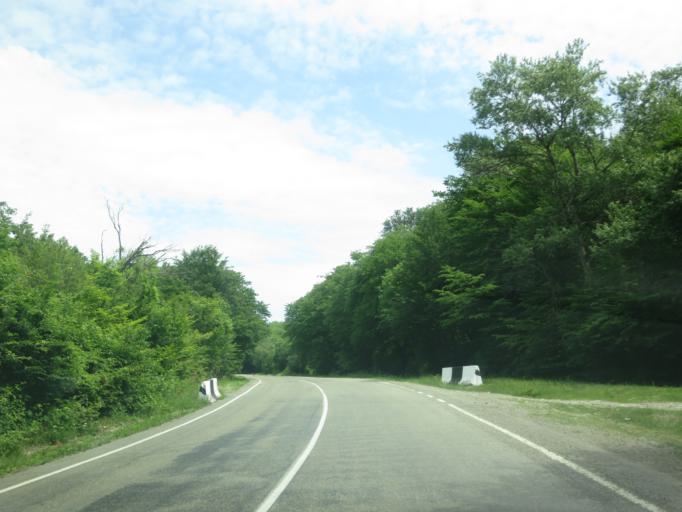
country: GE
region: Kakheti
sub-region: Telavi
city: Telavi
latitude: 41.9041
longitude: 45.3744
